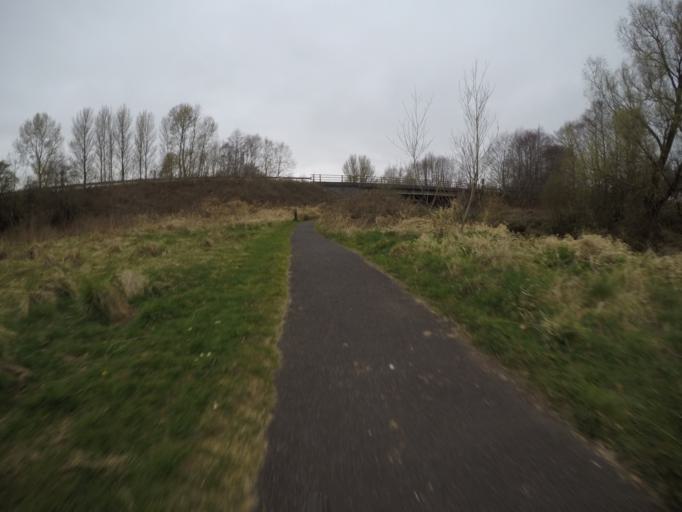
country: GB
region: Scotland
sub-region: North Ayrshire
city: Irvine
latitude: 55.6119
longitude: -4.6391
